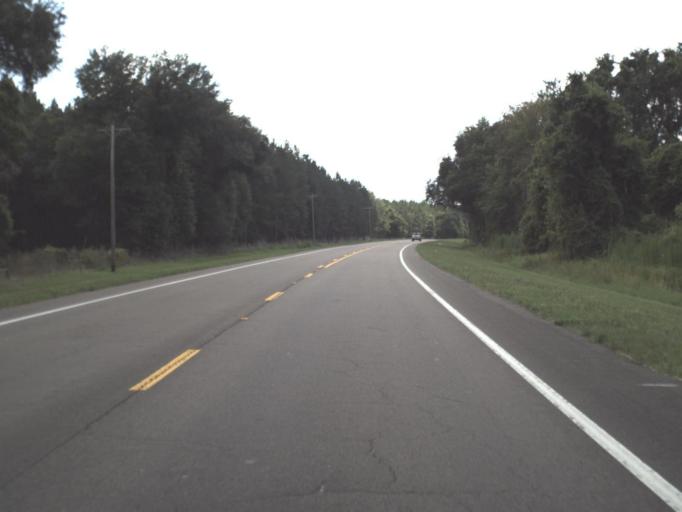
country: US
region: Florida
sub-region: Alachua County
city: Alachua
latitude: 29.8271
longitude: -82.3925
